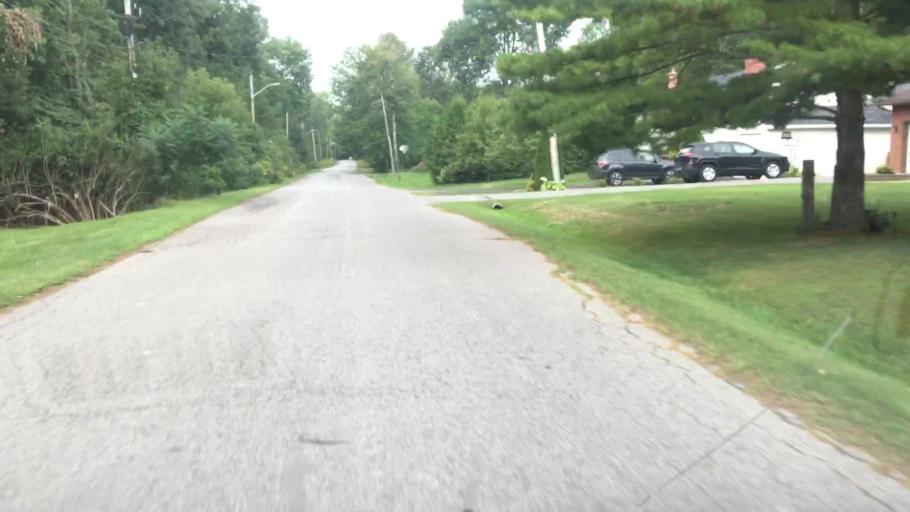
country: CA
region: Ontario
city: Quinte West
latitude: 44.0211
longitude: -77.7416
